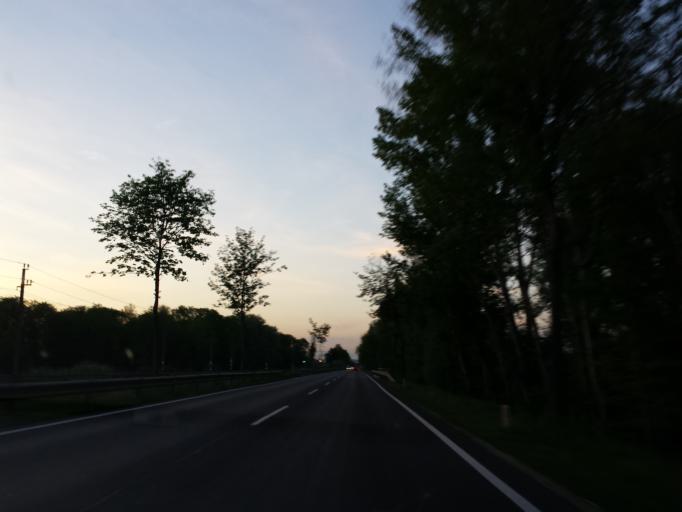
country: AT
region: Lower Austria
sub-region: Politischer Bezirk Tulln
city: Tulln
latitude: 48.3537
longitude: 16.0585
